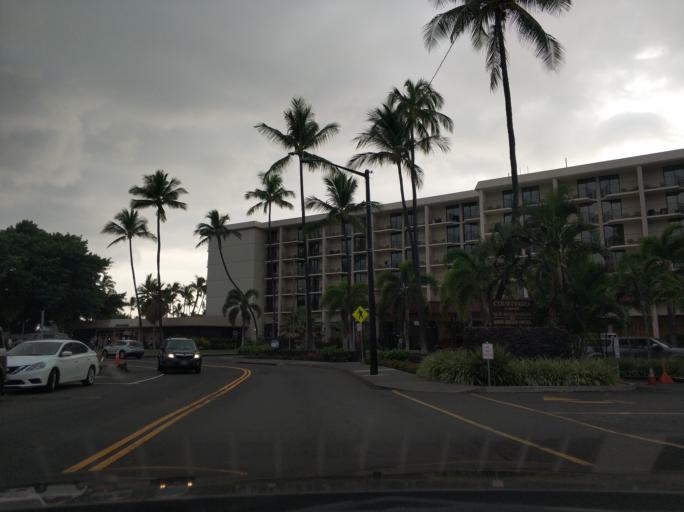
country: US
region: Hawaii
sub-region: Hawaii County
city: Kailua-Kona
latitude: 19.6411
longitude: -155.9969
